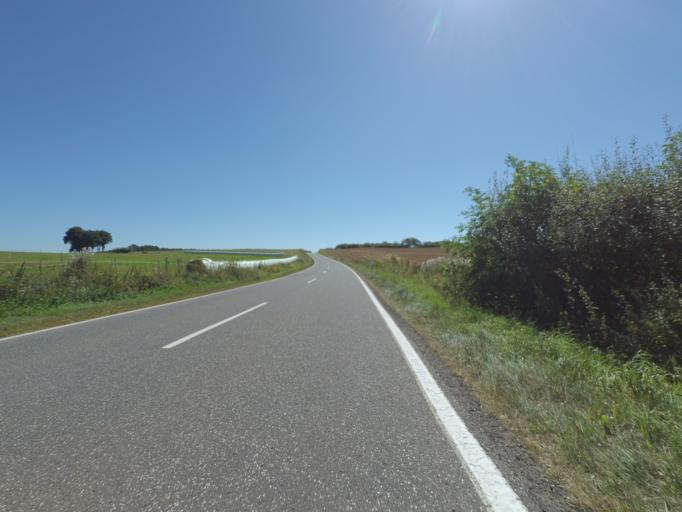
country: DE
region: Rheinland-Pfalz
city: Urschmitt
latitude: 50.1060
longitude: 7.0642
